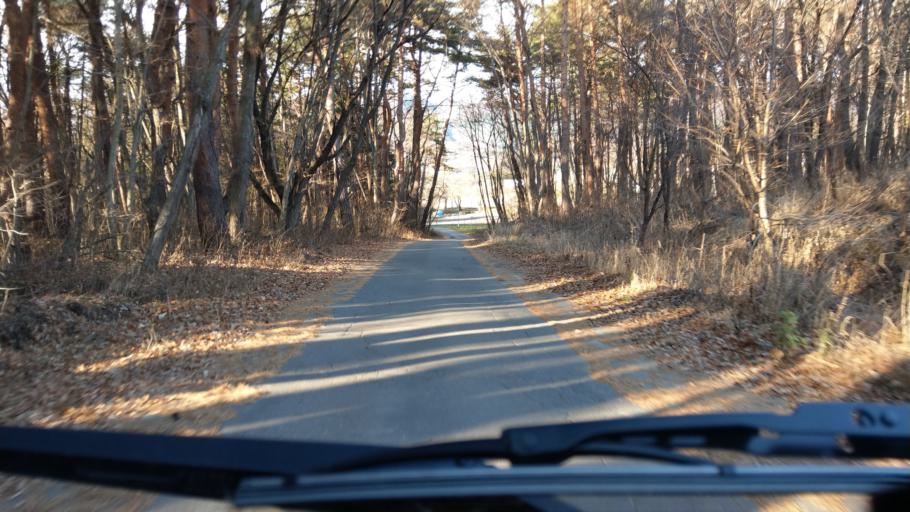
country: JP
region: Nagano
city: Komoro
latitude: 36.3484
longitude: 138.4495
